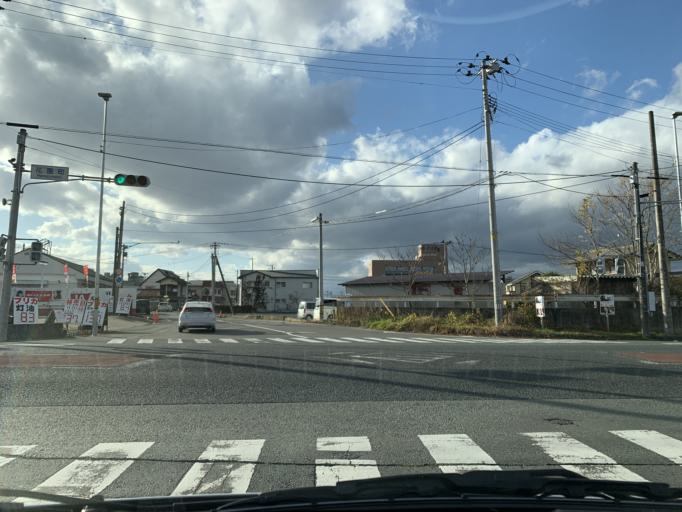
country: JP
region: Iwate
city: Mizusawa
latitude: 39.1411
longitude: 141.1501
